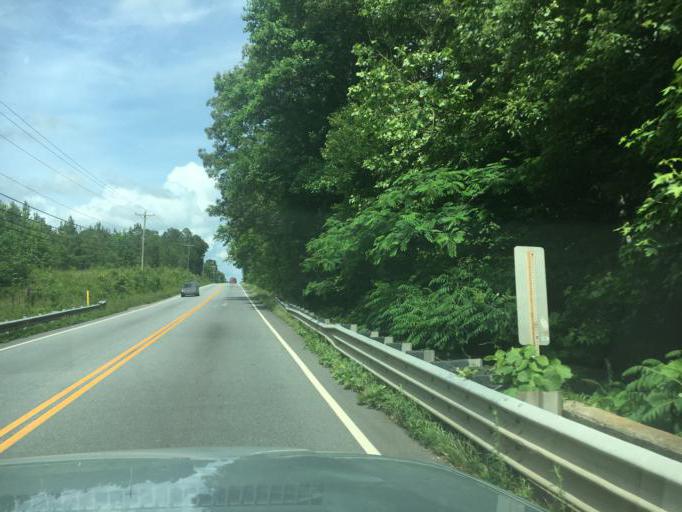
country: US
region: South Carolina
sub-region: Greenville County
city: Fountain Inn
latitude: 34.6703
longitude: -82.2402
